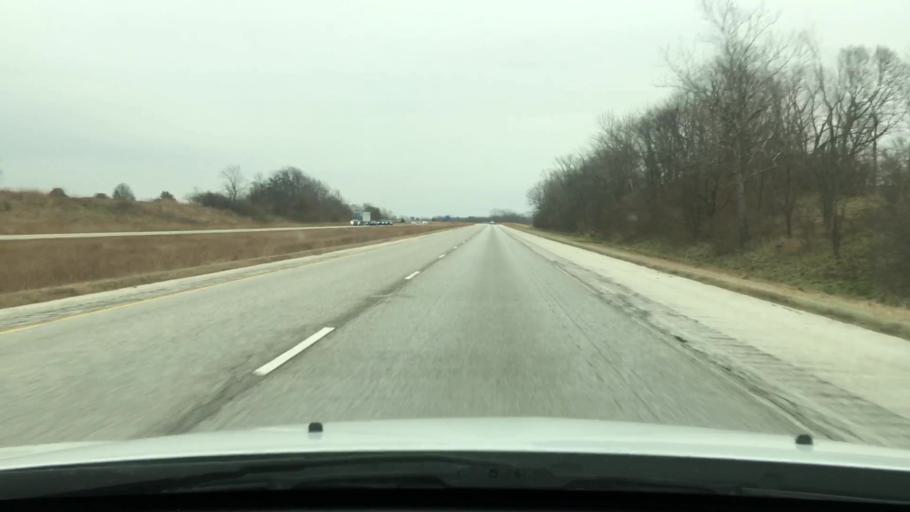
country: US
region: Illinois
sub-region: Morgan County
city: South Jacksonville
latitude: 39.6803
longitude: -90.2745
